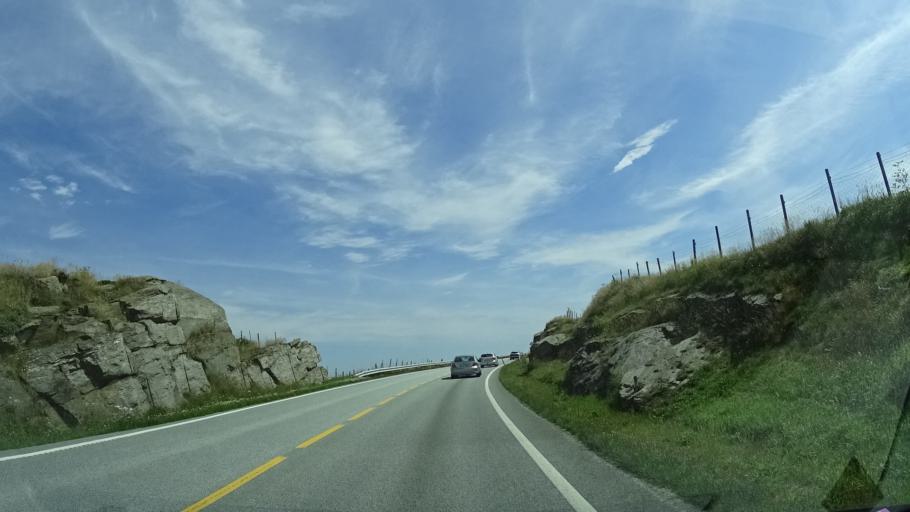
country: NO
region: Rogaland
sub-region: Rennesoy
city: Vikevag
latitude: 59.1380
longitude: 5.5979
